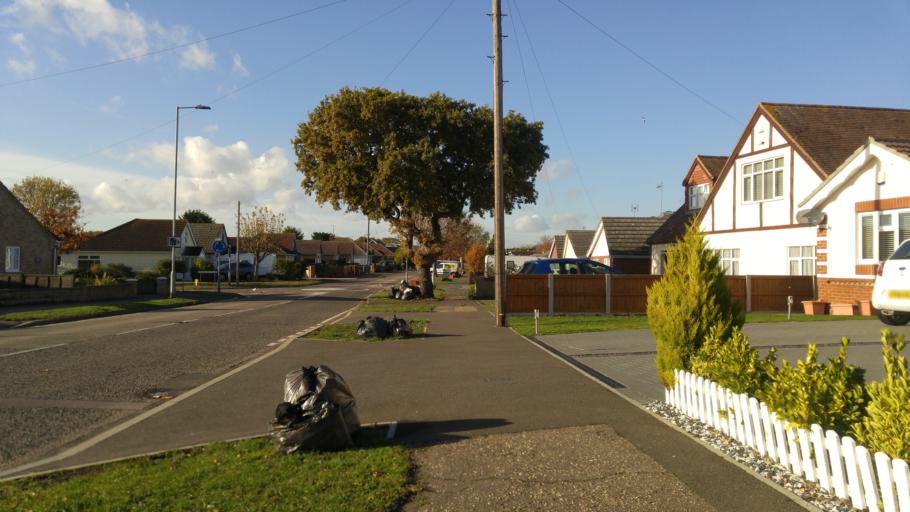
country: GB
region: England
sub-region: Essex
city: Clacton-on-Sea
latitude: 51.8145
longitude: 1.1715
